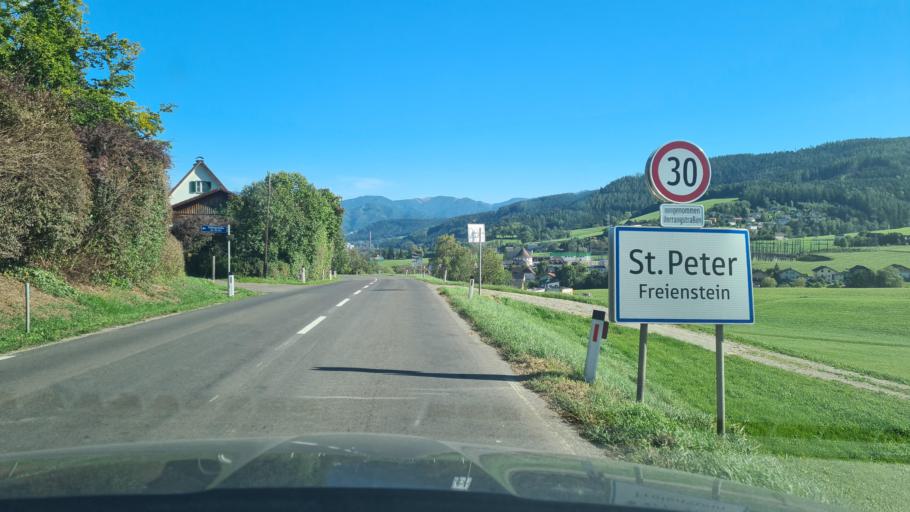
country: AT
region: Styria
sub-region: Politischer Bezirk Leoben
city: Sankt Peter-Freienstein
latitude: 47.4028
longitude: 15.0164
